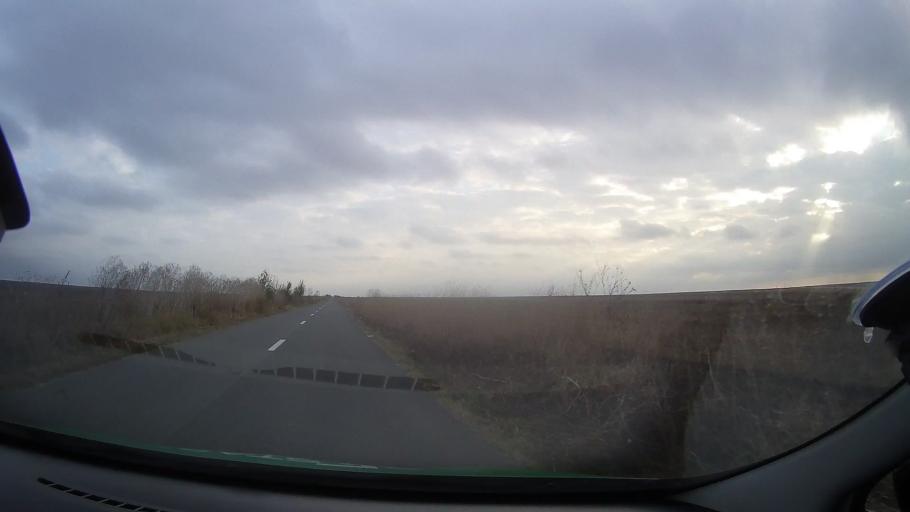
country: RO
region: Constanta
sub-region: Comuna Pestera
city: Pestera
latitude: 44.1471
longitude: 28.1149
